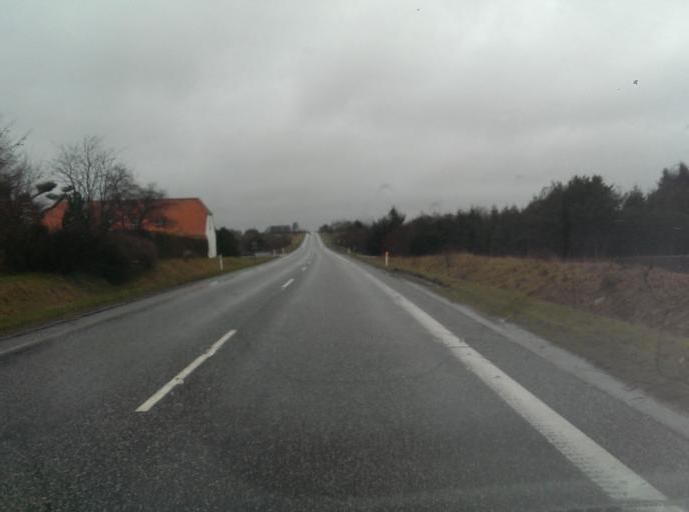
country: DK
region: Central Jutland
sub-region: Ringkobing-Skjern Kommune
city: Tarm
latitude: 55.7813
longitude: 8.4924
